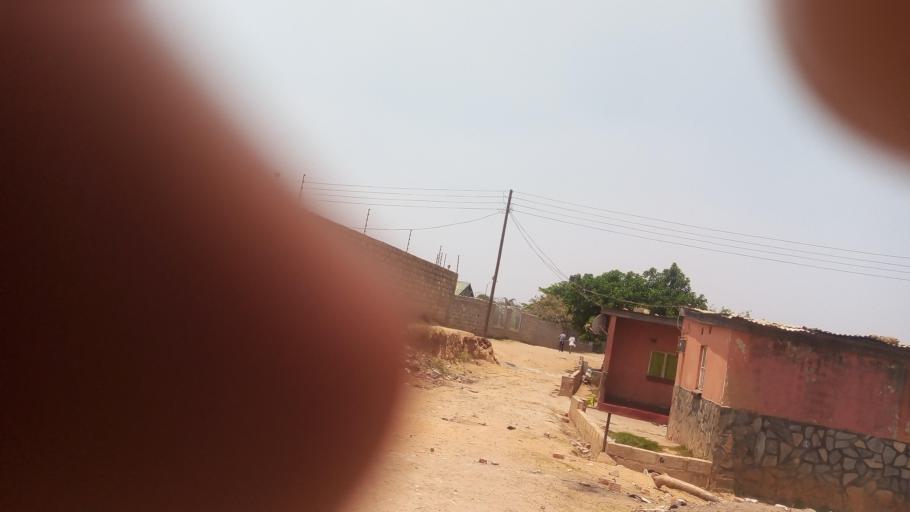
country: ZM
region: Lusaka
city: Lusaka
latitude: -15.4385
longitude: 28.3759
